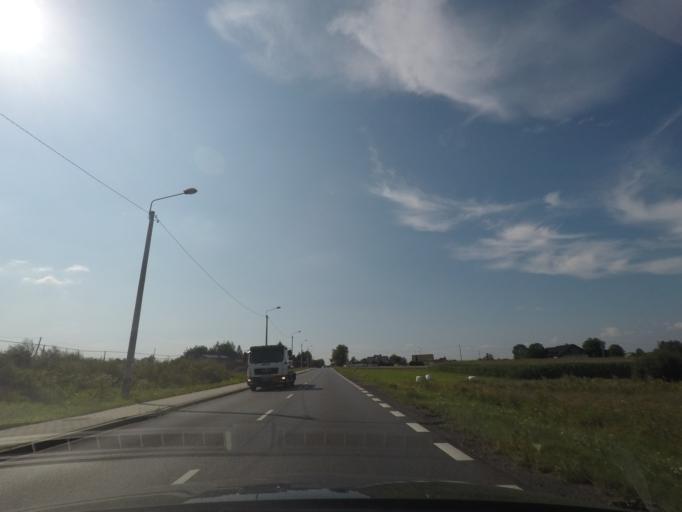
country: PL
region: Silesian Voivodeship
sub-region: Powiat pszczynski
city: Radostowice
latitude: 50.0033
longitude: 18.8771
